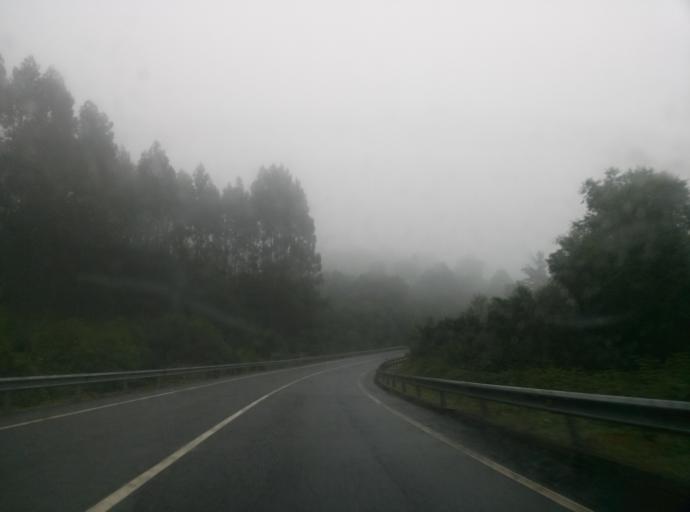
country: ES
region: Galicia
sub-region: Provincia de Lugo
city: Muras
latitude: 43.5094
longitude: -7.6753
